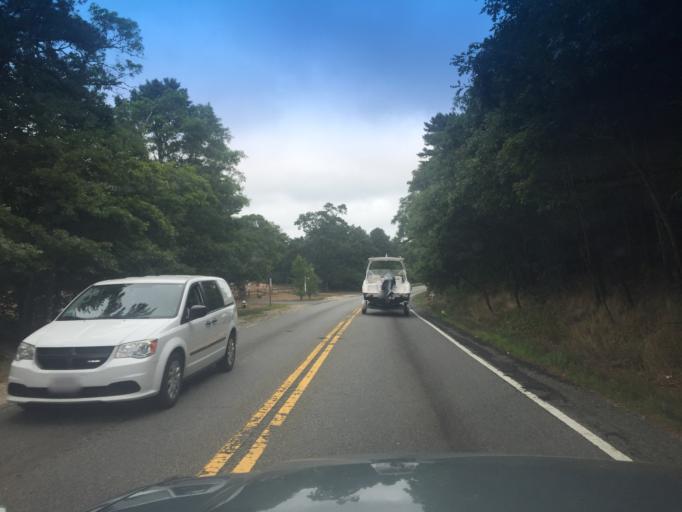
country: US
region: Massachusetts
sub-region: Barnstable County
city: Mashpee
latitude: 41.6240
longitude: -70.4788
